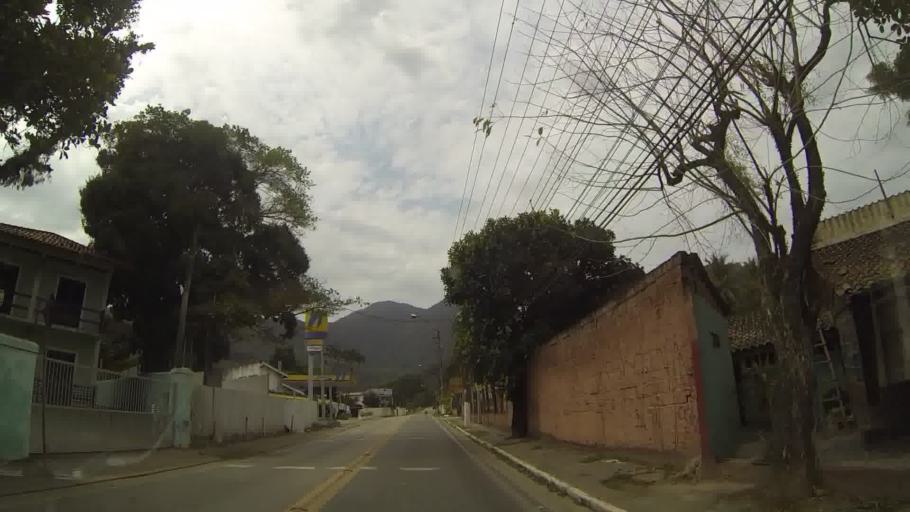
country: BR
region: Sao Paulo
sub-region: Sao Sebastiao
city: Sao Sebastiao
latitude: -23.7932
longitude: -45.5541
